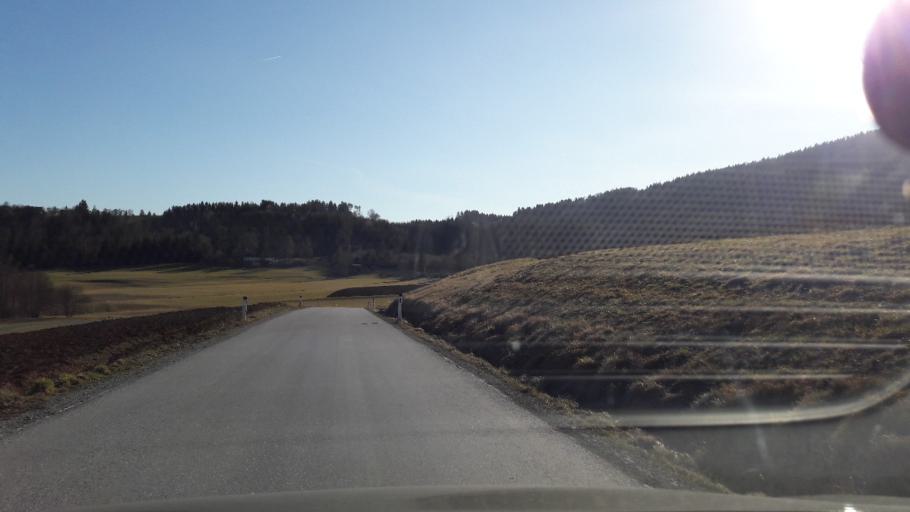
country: AT
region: Styria
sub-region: Politischer Bezirk Graz-Umgebung
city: Eisbach
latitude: 47.1246
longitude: 15.2872
